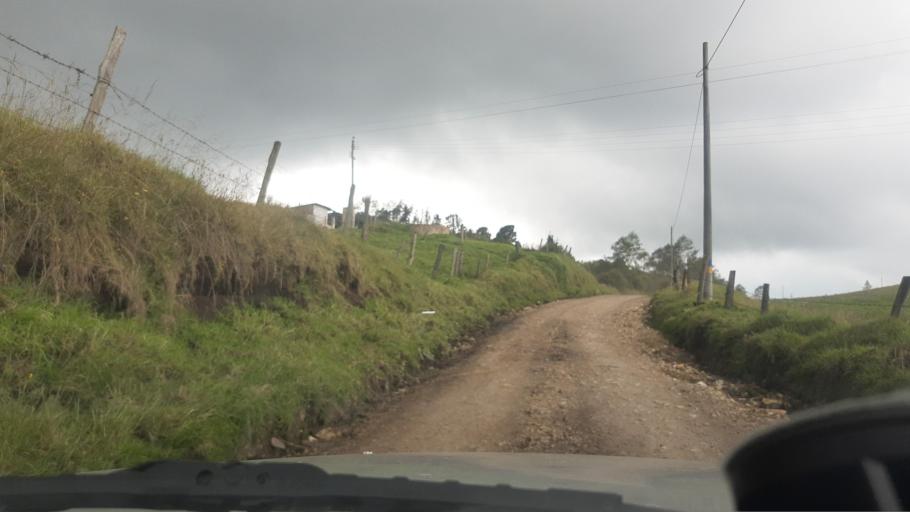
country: CO
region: Cundinamarca
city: Suesca
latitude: 5.1424
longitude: -73.7788
